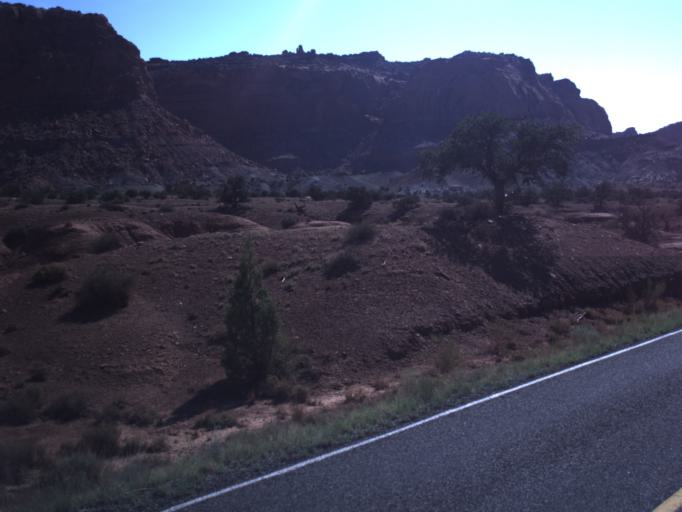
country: US
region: Utah
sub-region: Wayne County
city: Loa
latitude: 38.3193
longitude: -111.3146
